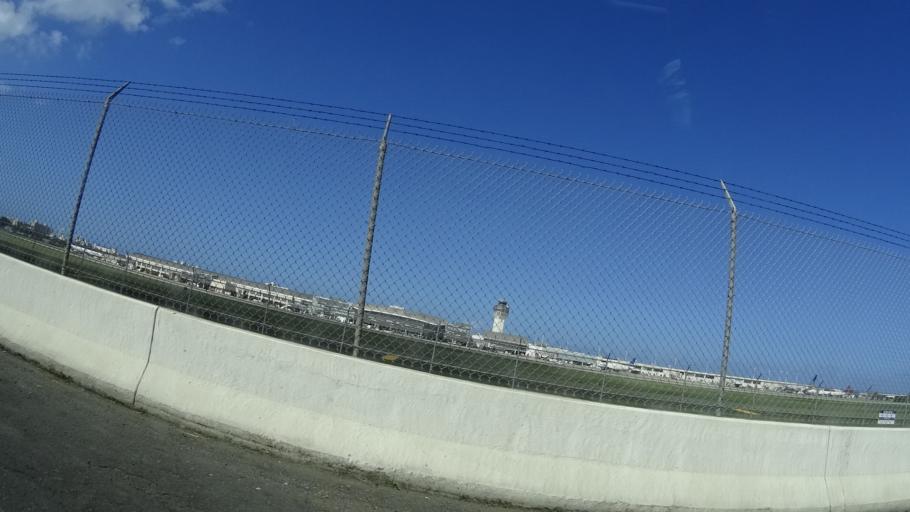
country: PR
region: Carolina
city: Carolina
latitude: 18.4320
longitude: -66.0043
